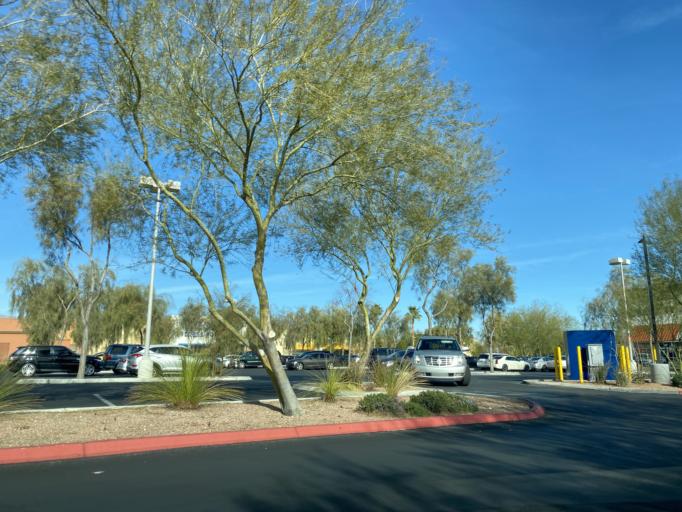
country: US
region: Nevada
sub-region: Clark County
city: North Las Vegas
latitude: 36.2719
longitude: -115.2087
